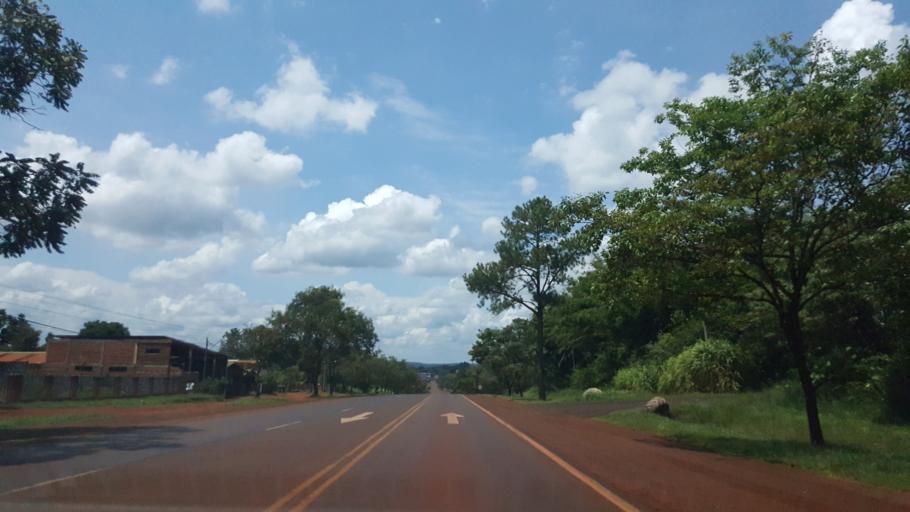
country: AR
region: Misiones
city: Garuhape
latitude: -26.8215
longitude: -54.9692
